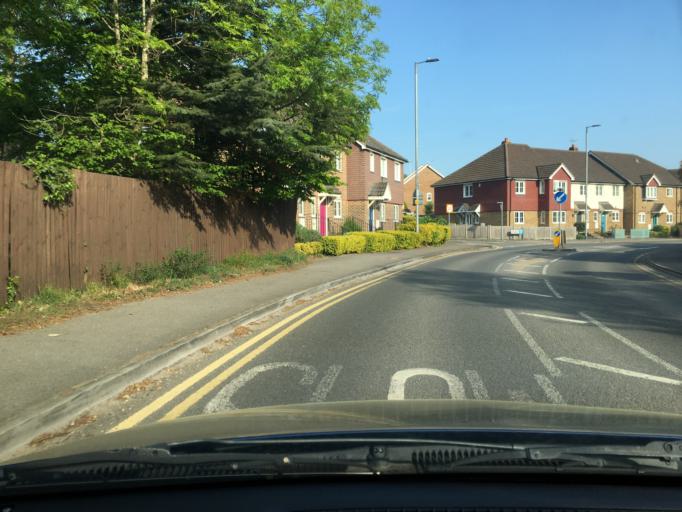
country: GB
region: England
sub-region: Hampshire
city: Yateley
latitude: 51.3483
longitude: -0.8109
